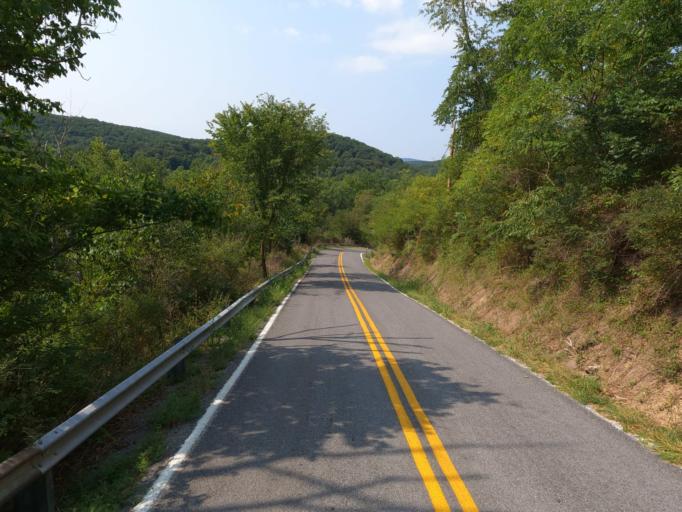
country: US
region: West Virginia
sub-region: Morgan County
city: Berkeley Springs
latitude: 39.6320
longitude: -78.3045
